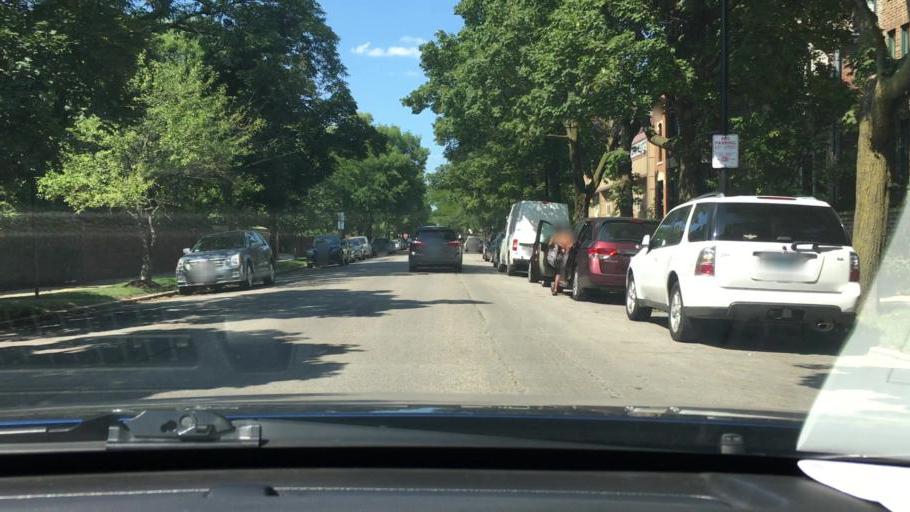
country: US
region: Illinois
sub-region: Cook County
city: Chicago
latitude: 41.9166
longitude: -87.6436
